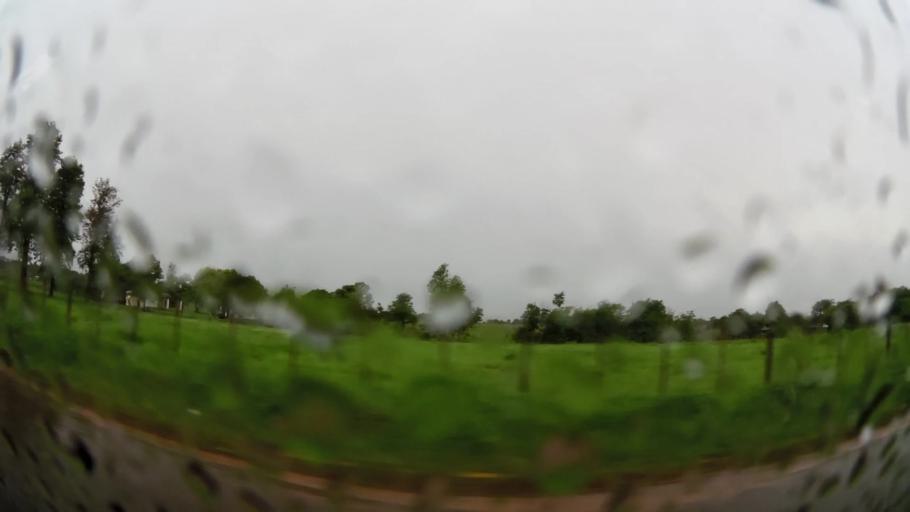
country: PY
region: Alto Parana
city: Presidente Franco
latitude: -25.5267
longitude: -54.6781
